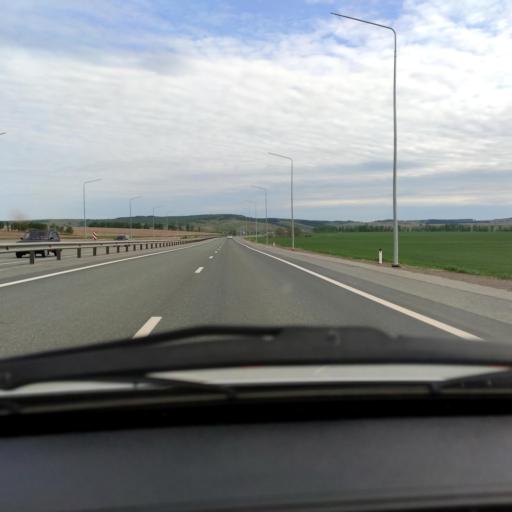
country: RU
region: Bashkortostan
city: Tolbazy
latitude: 54.0549
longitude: 55.8885
